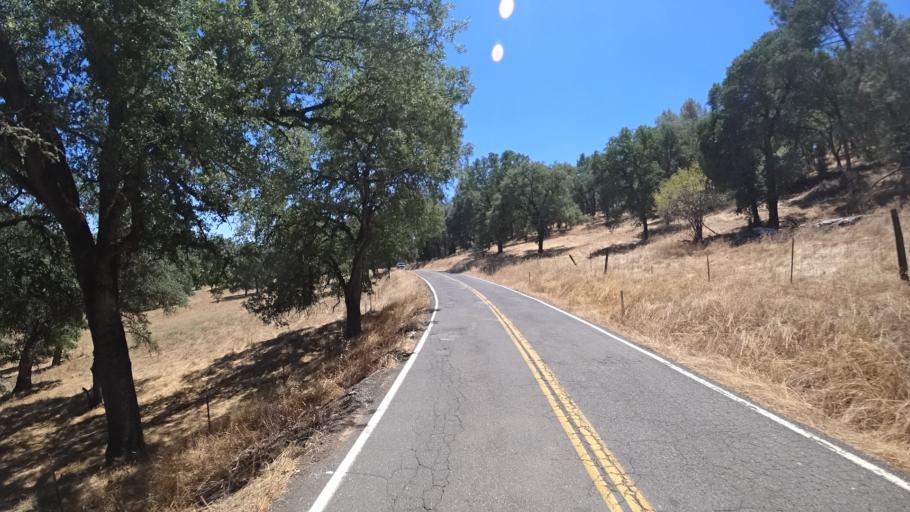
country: US
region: California
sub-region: Calaveras County
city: San Andreas
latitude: 38.1320
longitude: -120.6641
